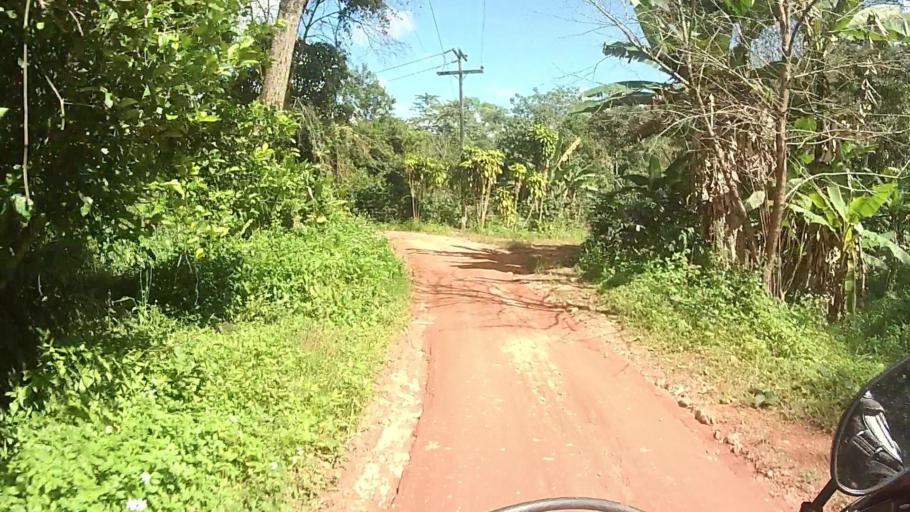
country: TH
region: Lampang
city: Mueang Pan
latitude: 18.9109
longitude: 99.4119
